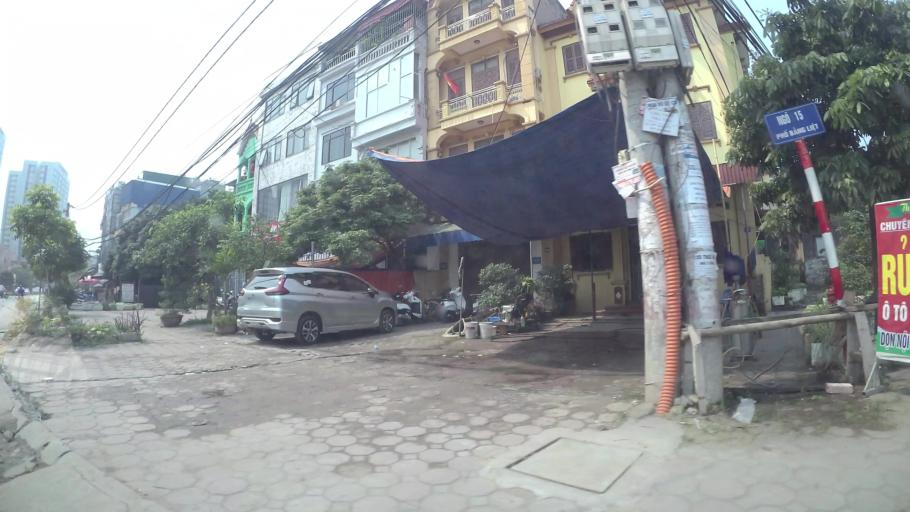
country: VN
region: Ha Noi
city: Van Dien
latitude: 20.9647
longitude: 105.8206
